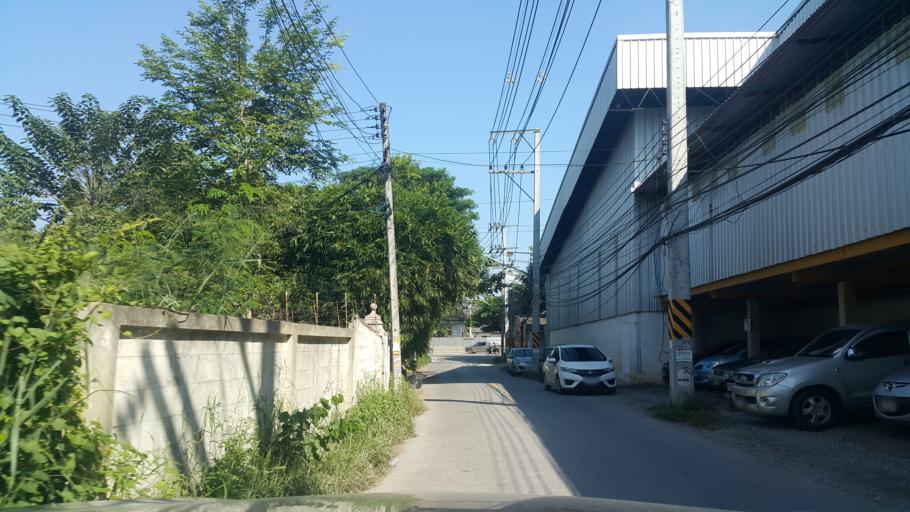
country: TH
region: Chiang Mai
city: Chiang Mai
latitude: 18.8079
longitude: 99.0127
